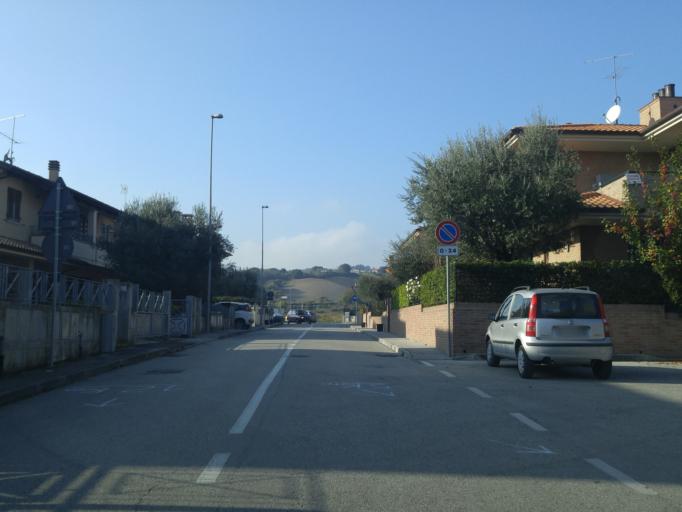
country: IT
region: The Marches
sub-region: Provincia di Pesaro e Urbino
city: Calcinelli
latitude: 43.7571
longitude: 12.9187
